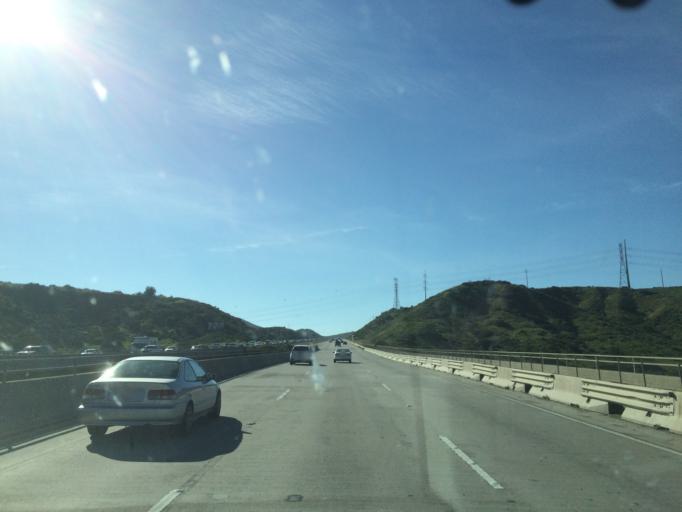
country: US
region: California
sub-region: San Diego County
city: Santee
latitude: 32.8513
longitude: -117.0370
